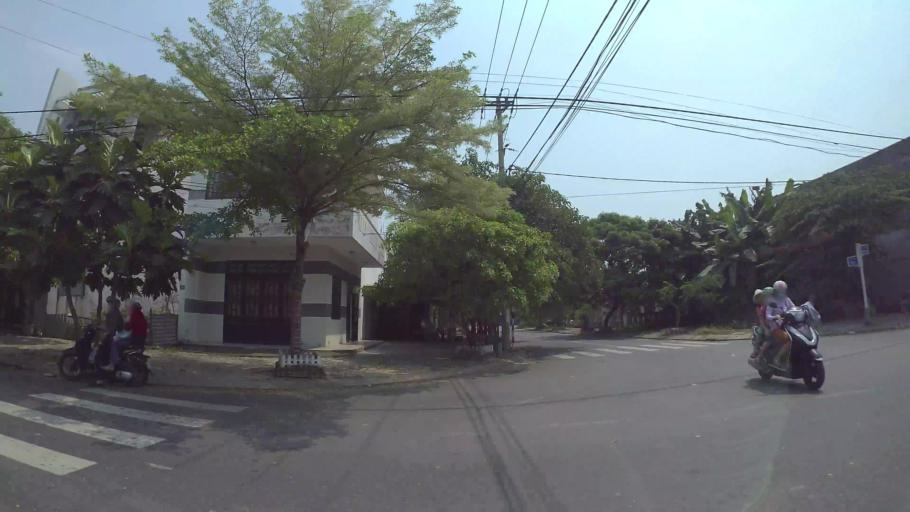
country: VN
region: Da Nang
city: Cam Le
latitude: 16.0049
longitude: 108.2129
